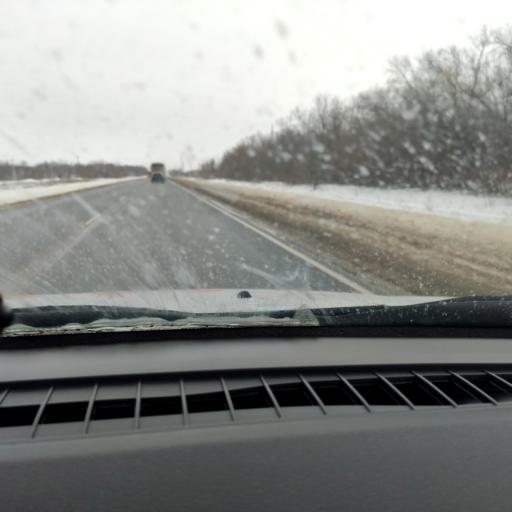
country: RU
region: Samara
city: Dubovyy Umet
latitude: 52.9812
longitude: 50.2690
